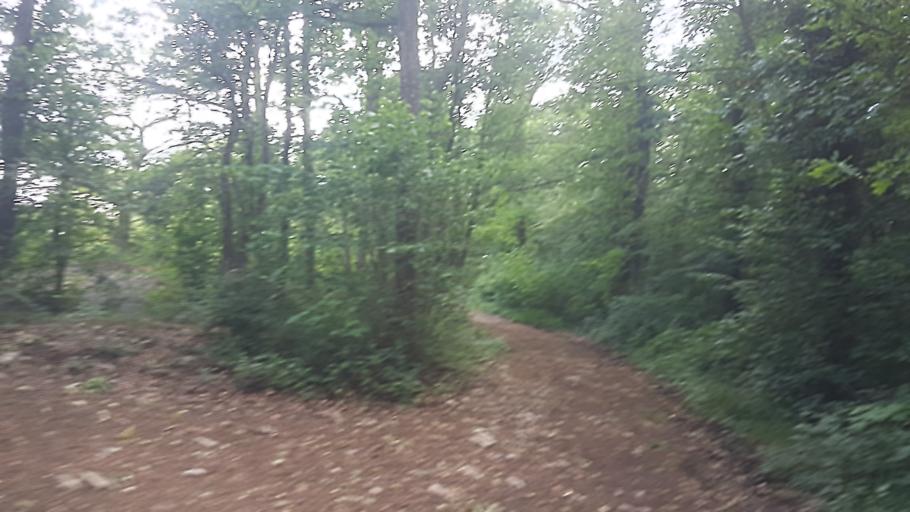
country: BE
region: Wallonia
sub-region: Province de Namur
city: Couvin
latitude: 50.0783
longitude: 4.5987
